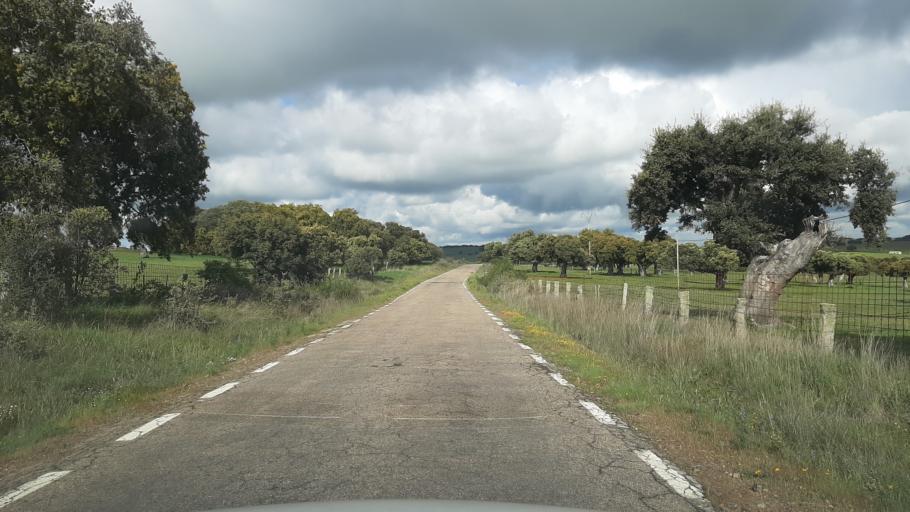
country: ES
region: Castille and Leon
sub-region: Provincia de Salamanca
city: Narros de Matalayegua
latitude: 40.7032
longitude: -5.9119
